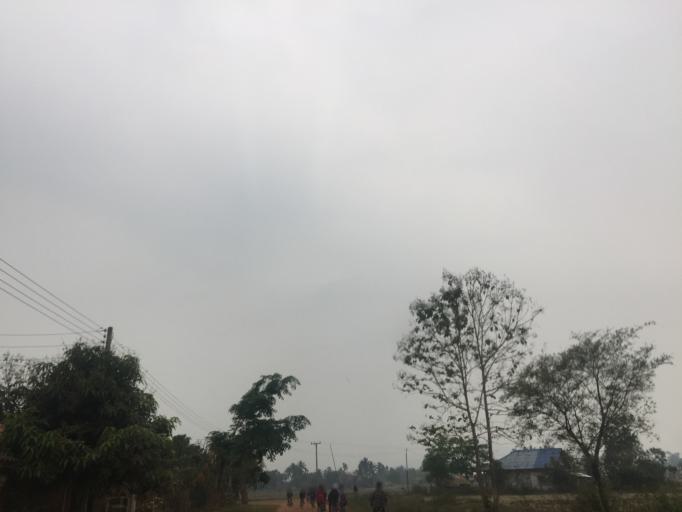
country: LA
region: Xiagnabouli
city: Sainyabuli
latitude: 19.0060
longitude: 101.5094
